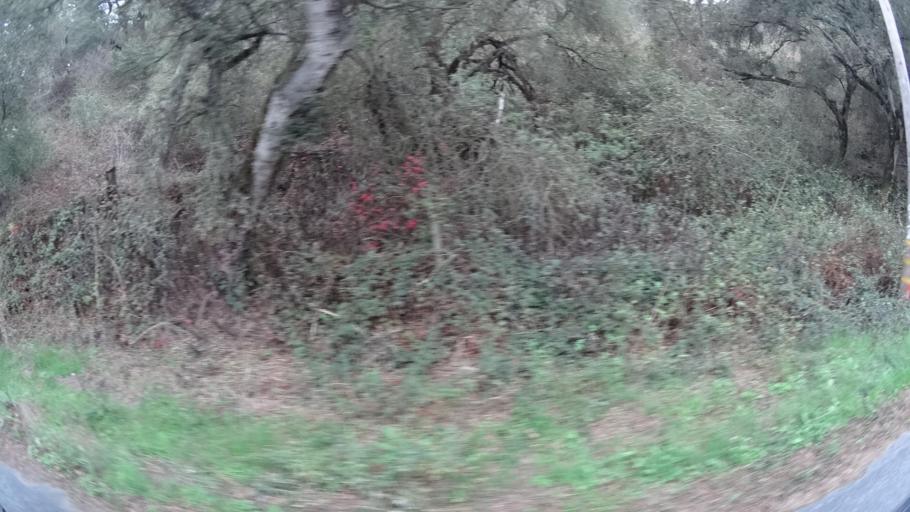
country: US
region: California
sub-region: Monterey County
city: Las Lomas
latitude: 36.8793
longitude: -121.7425
